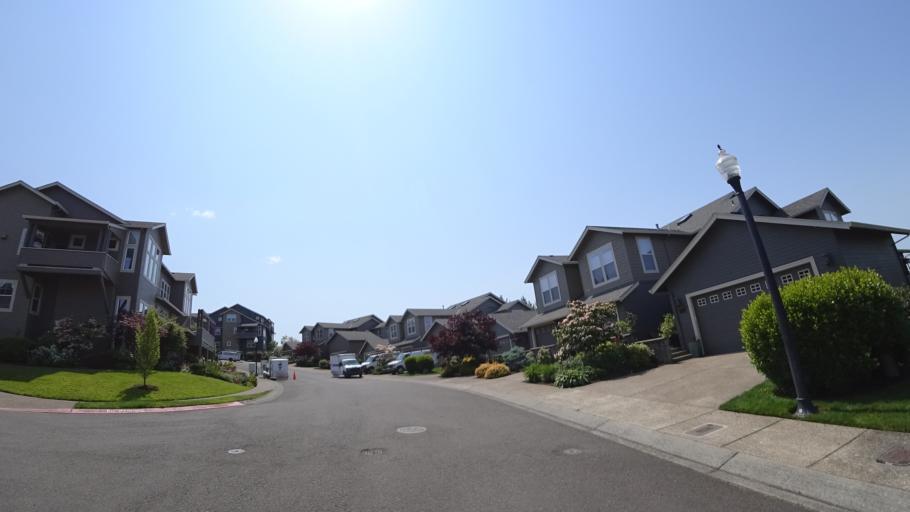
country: US
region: Oregon
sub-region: Multnomah County
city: Lents
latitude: 45.4598
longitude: -122.5582
